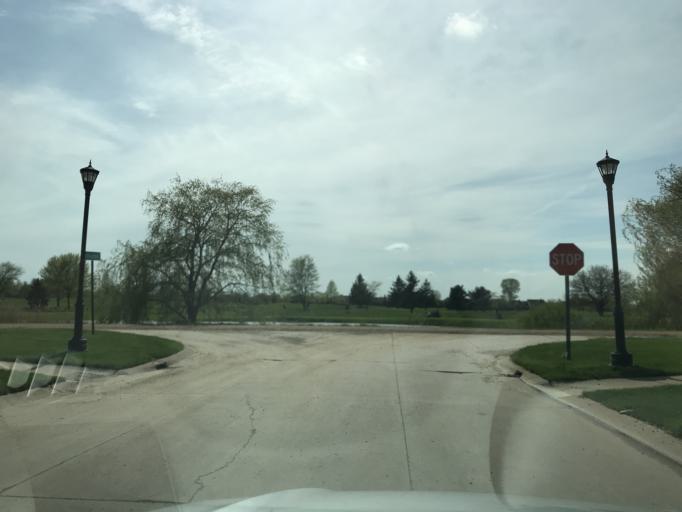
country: US
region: Michigan
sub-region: Oakland County
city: Wixom
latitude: 42.4605
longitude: -83.5726
